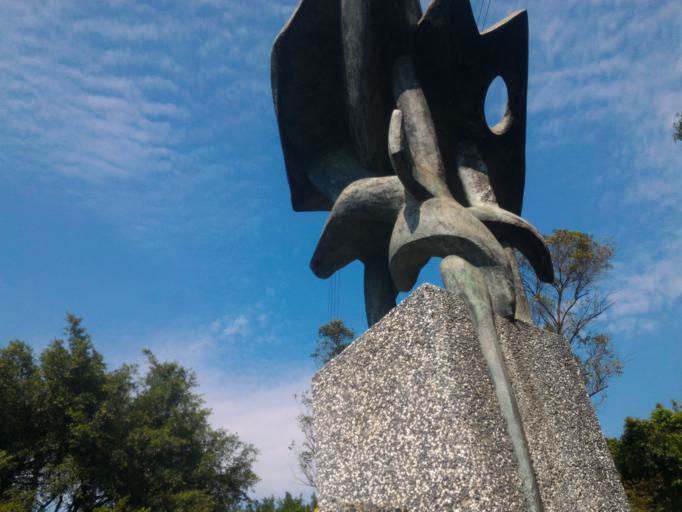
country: TW
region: Taipei
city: Taipei
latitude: 25.0416
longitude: 121.6164
